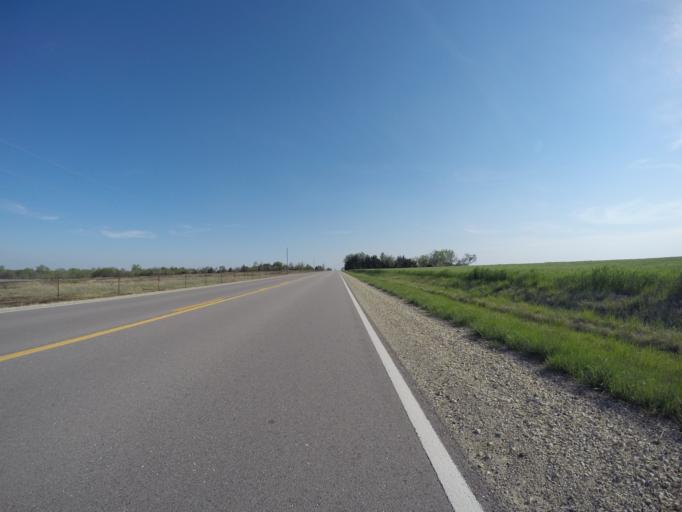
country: US
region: Kansas
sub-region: Riley County
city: Fort Riley North
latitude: 39.2868
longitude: -96.7751
